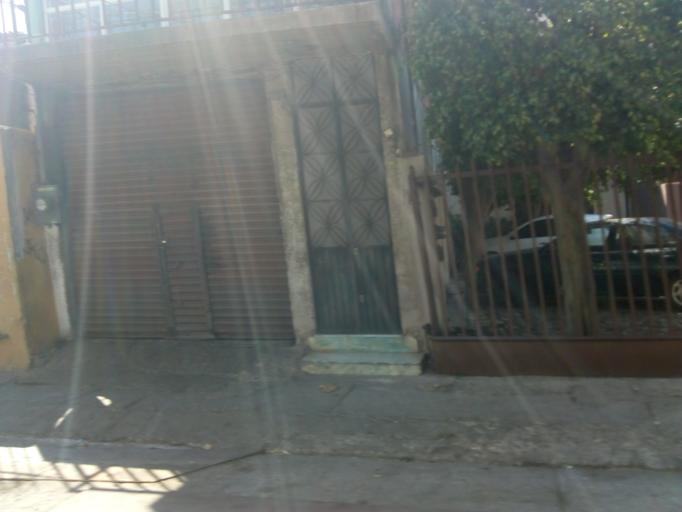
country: MX
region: Guanajuato
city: Leon
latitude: 21.1371
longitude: -101.6852
